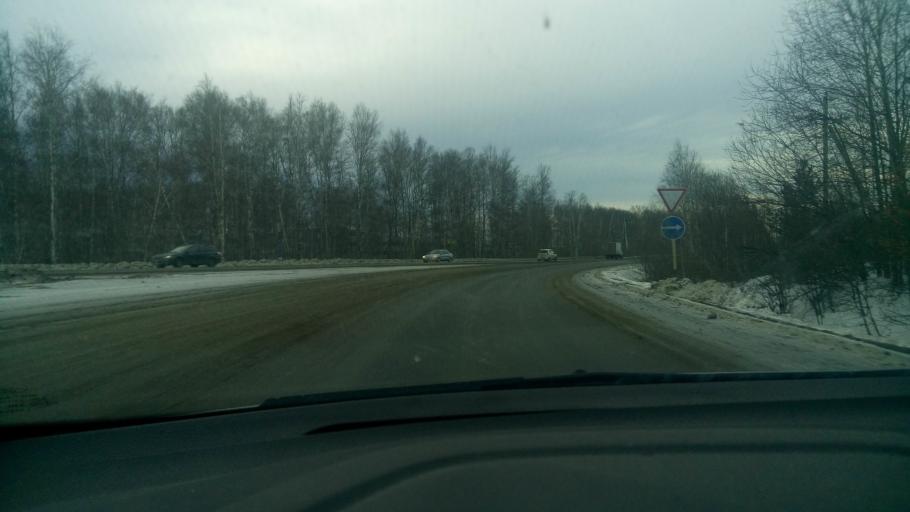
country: RU
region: Sverdlovsk
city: Istok
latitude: 56.7587
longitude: 60.7647
